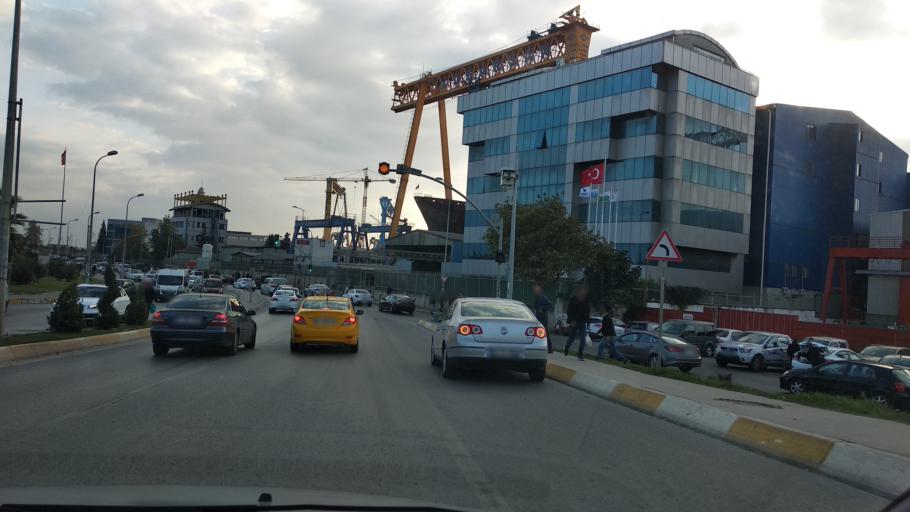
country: TR
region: Istanbul
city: Icmeler
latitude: 40.8465
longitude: 29.2938
